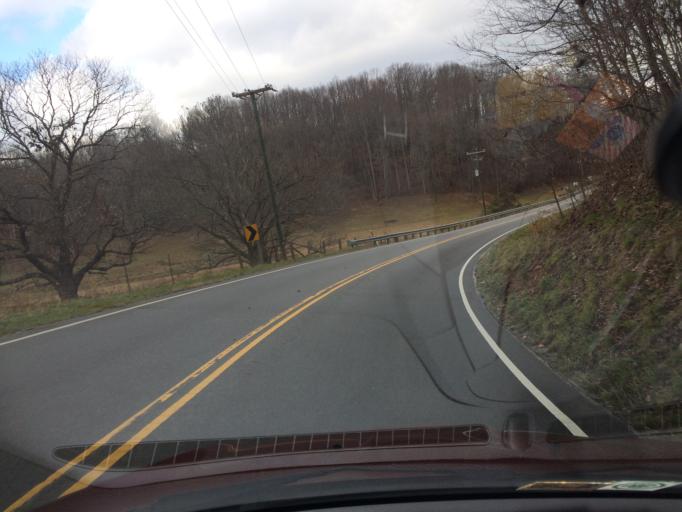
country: US
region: Virginia
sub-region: Patrick County
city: Stuart
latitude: 36.7510
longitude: -80.2682
